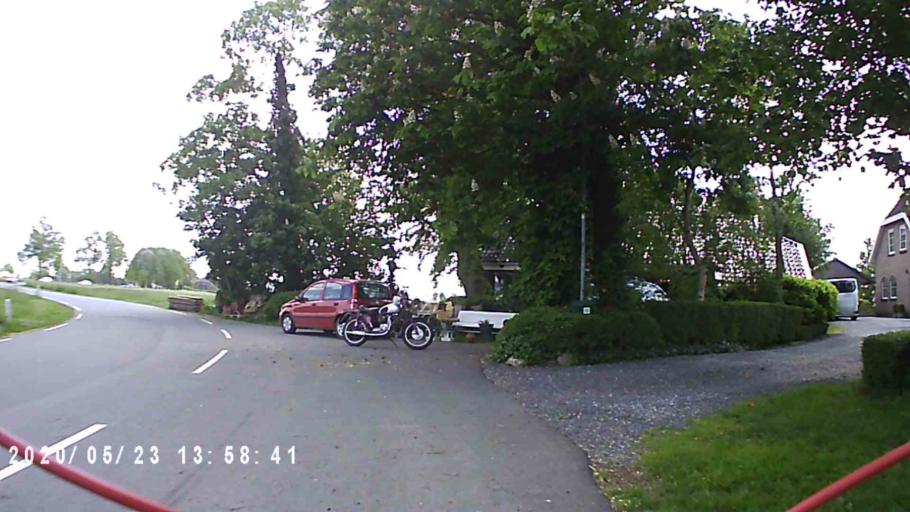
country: NL
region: Groningen
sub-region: Gemeente  Oldambt
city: Winschoten
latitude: 53.2620
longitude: 7.0260
